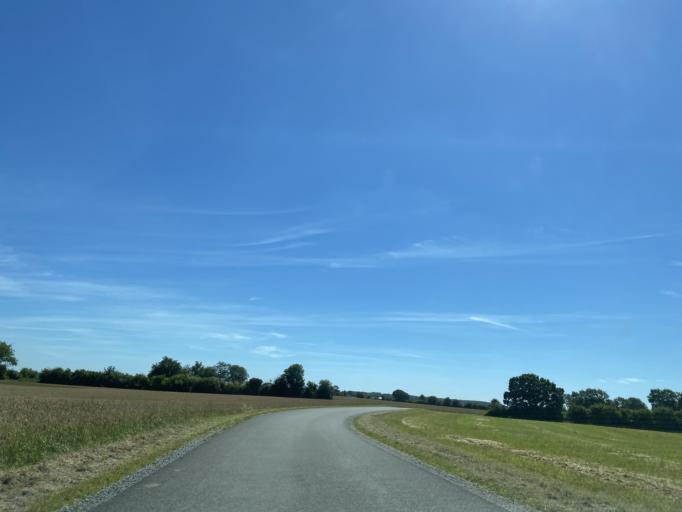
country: DK
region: South Denmark
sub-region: Vejle Kommune
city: Vejle
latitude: 55.6118
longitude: 9.5342
